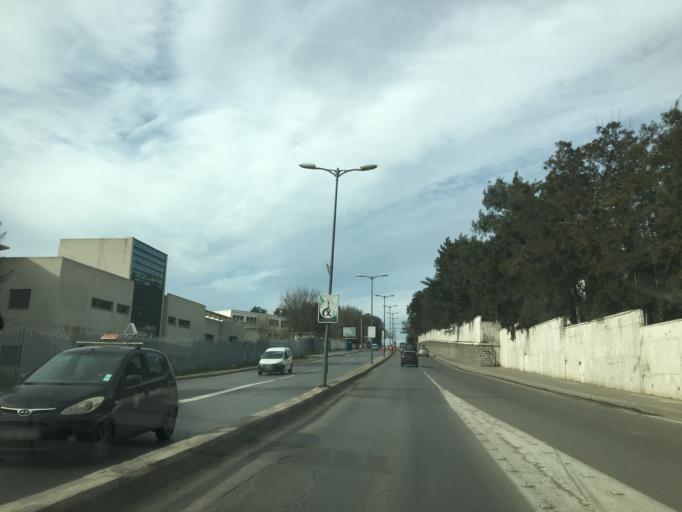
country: DZ
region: Alger
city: Algiers
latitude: 36.7688
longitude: 3.0183
